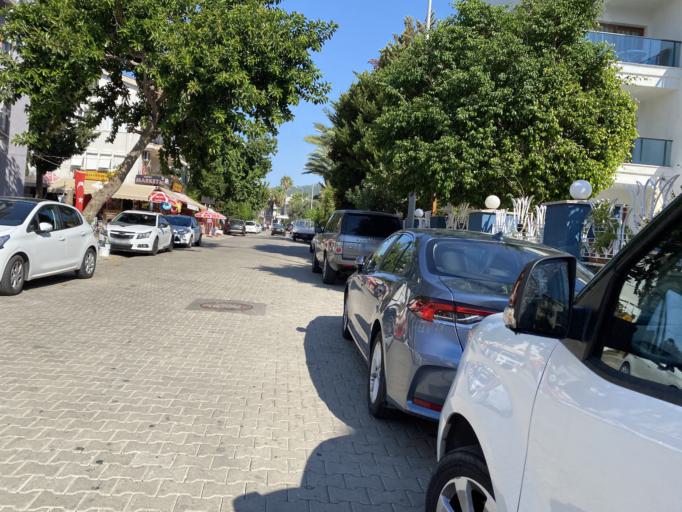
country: TR
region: Mugla
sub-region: Marmaris
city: Marmaris
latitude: 36.8441
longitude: 28.2529
